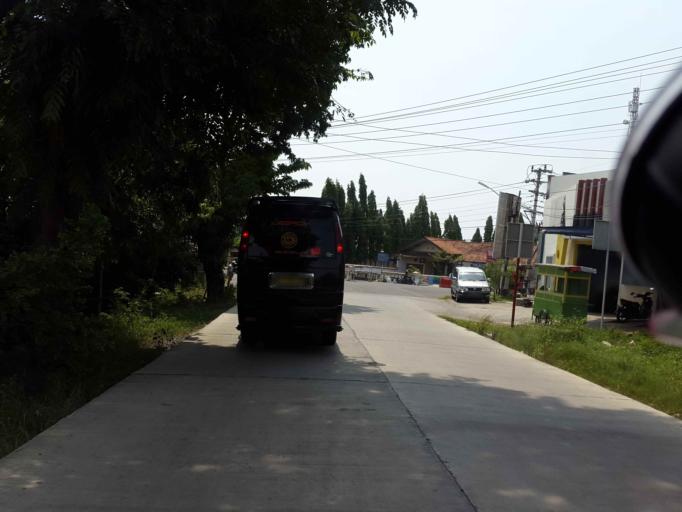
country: ID
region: Central Java
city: Pemalang
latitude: -6.9036
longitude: 109.3885
